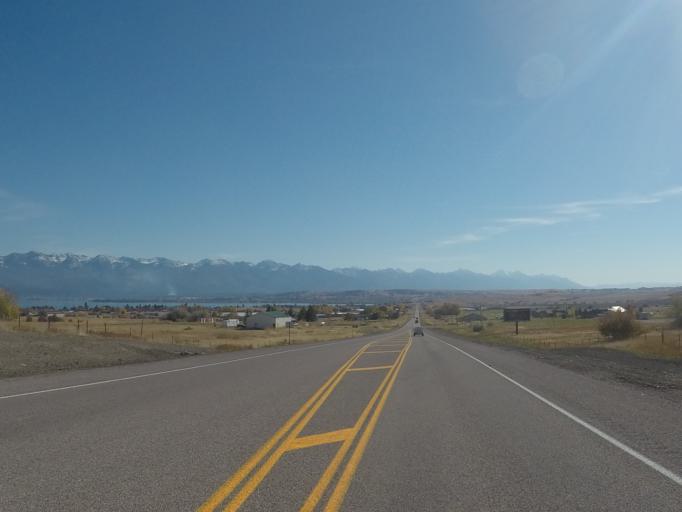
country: US
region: Montana
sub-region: Lake County
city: Polson
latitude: 47.7313
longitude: -114.2155
